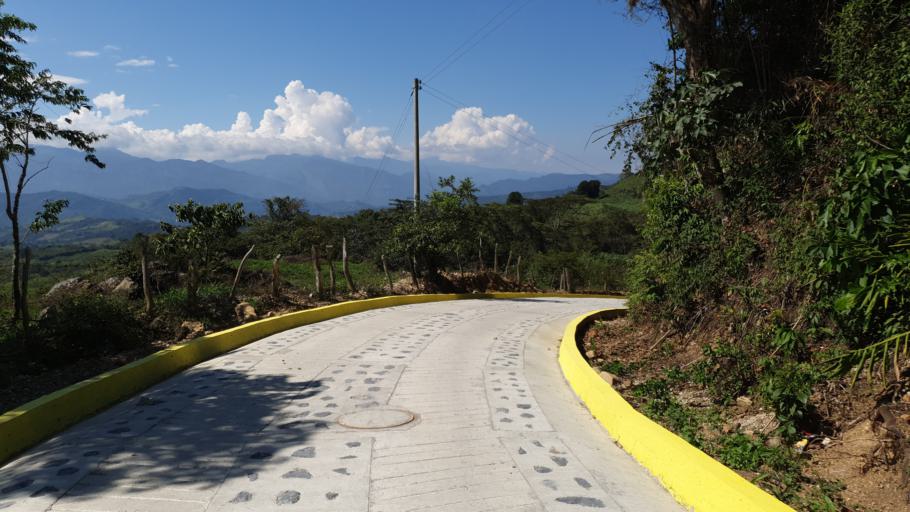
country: CO
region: Boyaca
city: Santana
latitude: 6.0534
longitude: -73.4866
